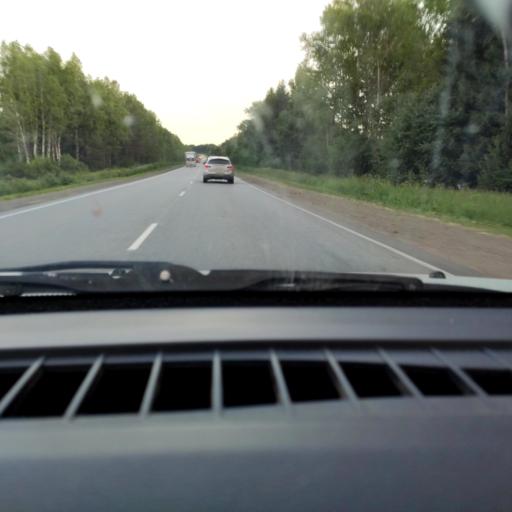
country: RU
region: Perm
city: Kungur
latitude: 57.4640
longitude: 56.7569
